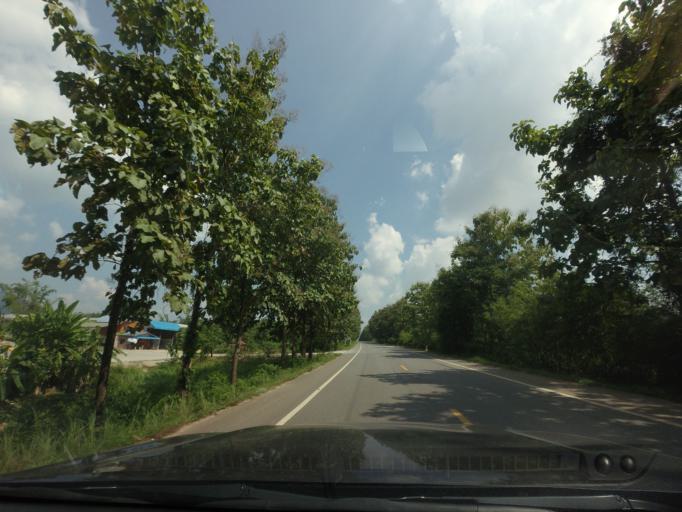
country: TH
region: Phitsanulok
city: Chat Trakan
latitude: 17.2875
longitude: 100.5197
